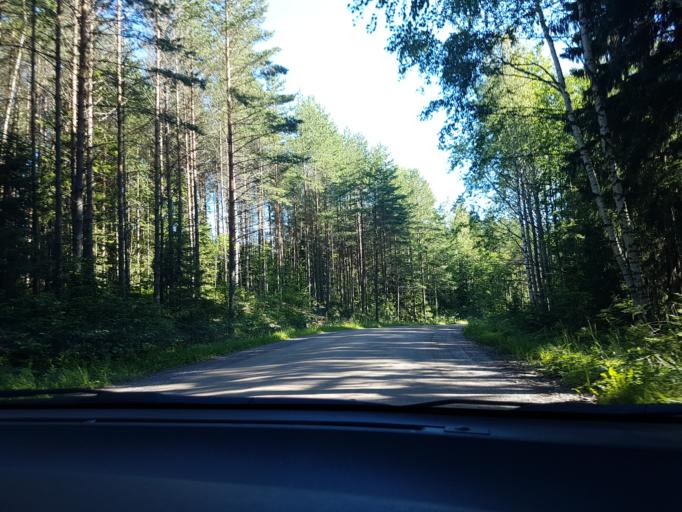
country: FI
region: Uusimaa
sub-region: Helsinki
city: Sibbo
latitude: 60.2704
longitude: 25.2303
